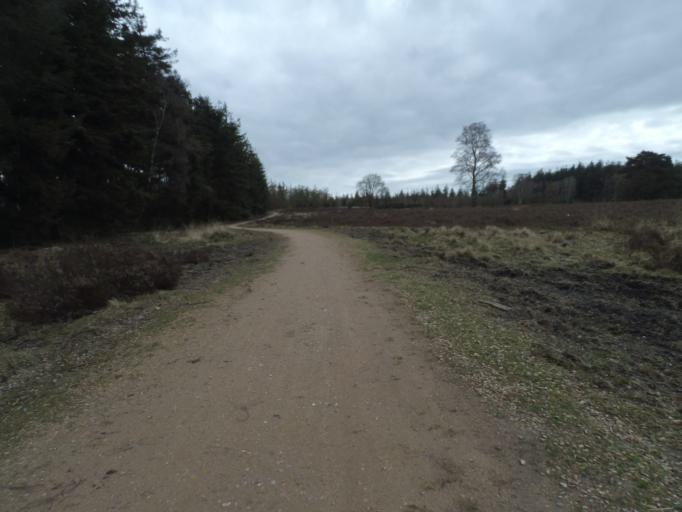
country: NL
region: Gelderland
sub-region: Gemeente Apeldoorn
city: Loenen
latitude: 52.0868
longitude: 5.9879
